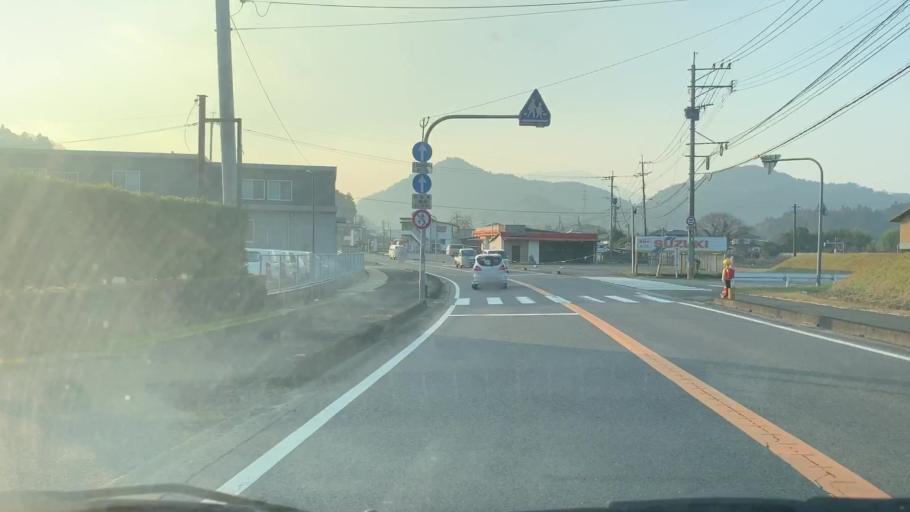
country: JP
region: Saga Prefecture
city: Takeocho-takeo
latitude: 33.2728
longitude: 130.1197
